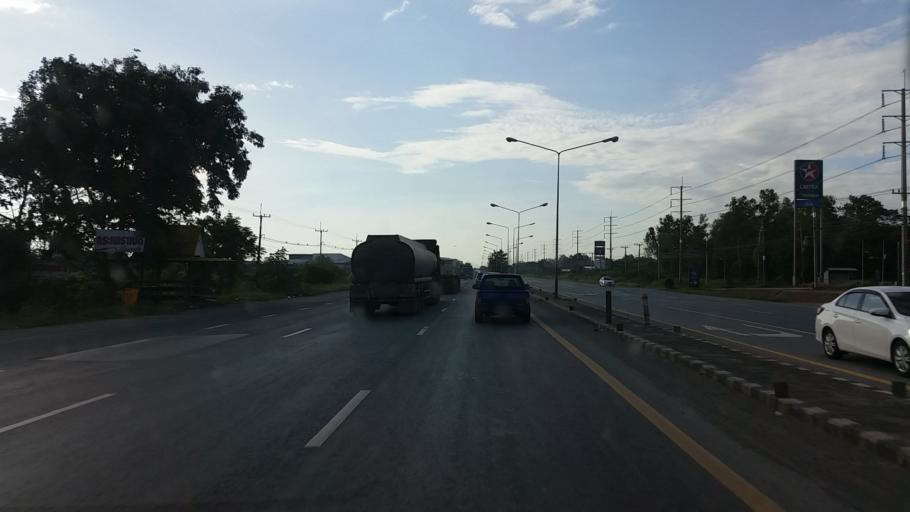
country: TH
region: Sara Buri
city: Chaloem Phra Kiat
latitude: 14.5976
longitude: 100.8967
